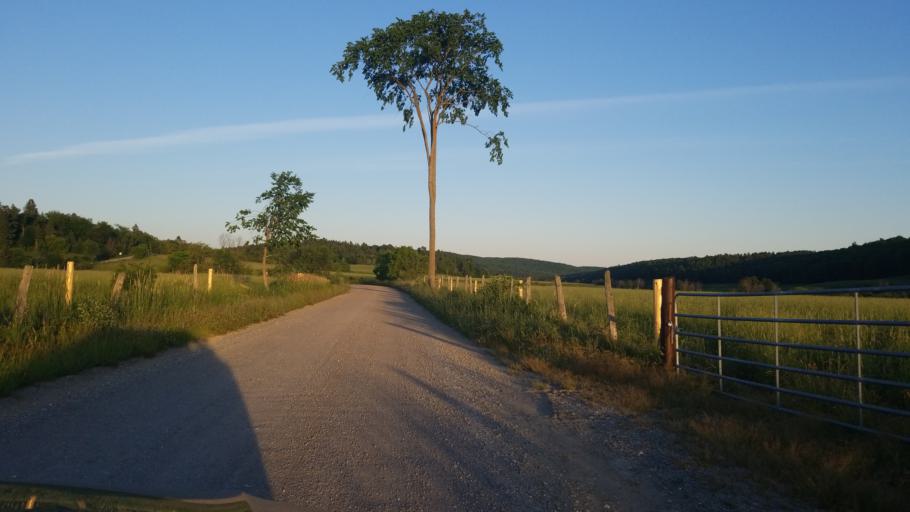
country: CA
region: Quebec
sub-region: Outaouais
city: Wakefield
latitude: 45.5834
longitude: -75.8991
